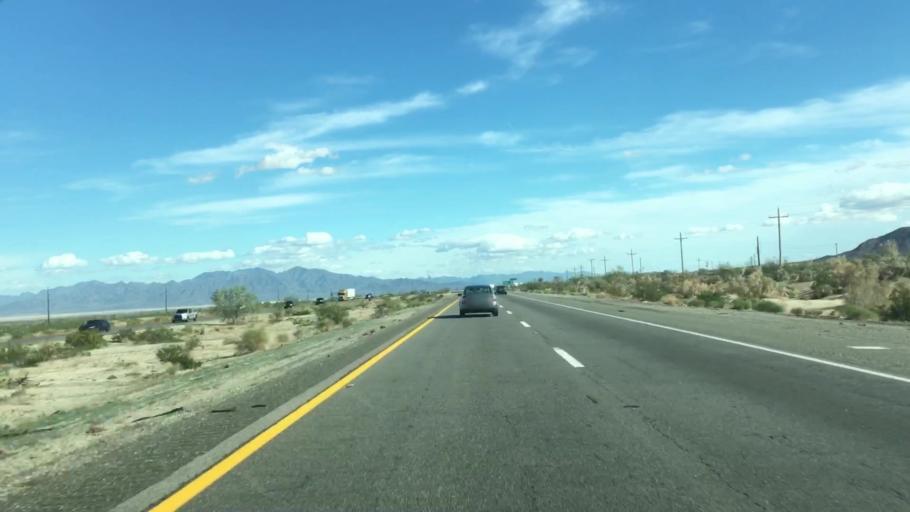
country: US
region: California
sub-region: Imperial County
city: Niland
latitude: 33.7105
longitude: -115.3853
